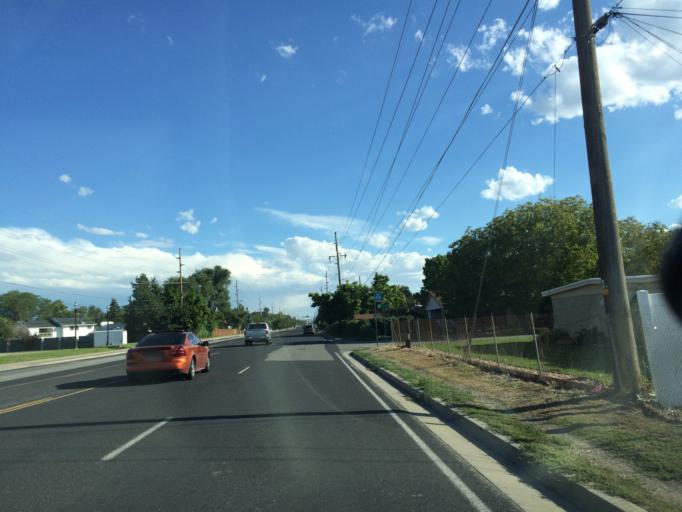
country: US
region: Utah
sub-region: Salt Lake County
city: Taylorsville
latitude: 40.6890
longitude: -111.9580
